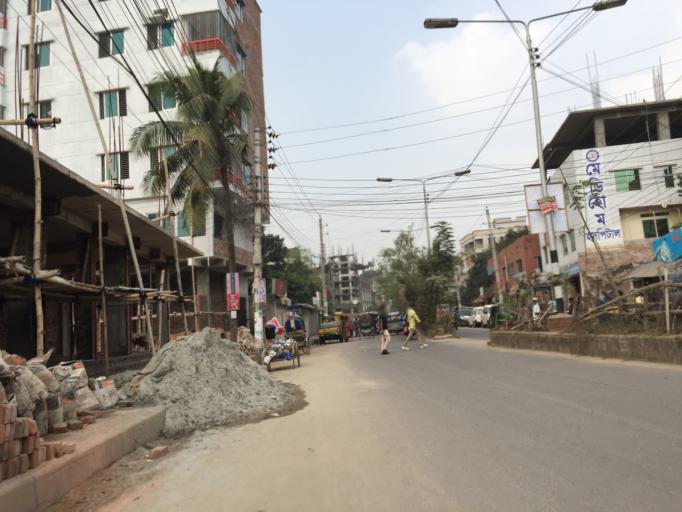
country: BD
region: Dhaka
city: Azimpur
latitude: 23.7906
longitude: 90.3661
